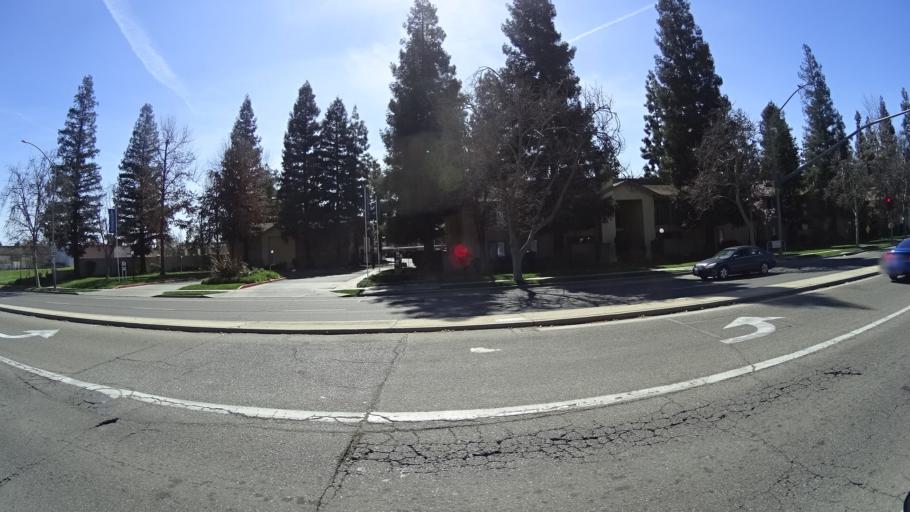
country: US
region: California
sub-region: Fresno County
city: Clovis
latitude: 36.8519
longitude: -119.7961
